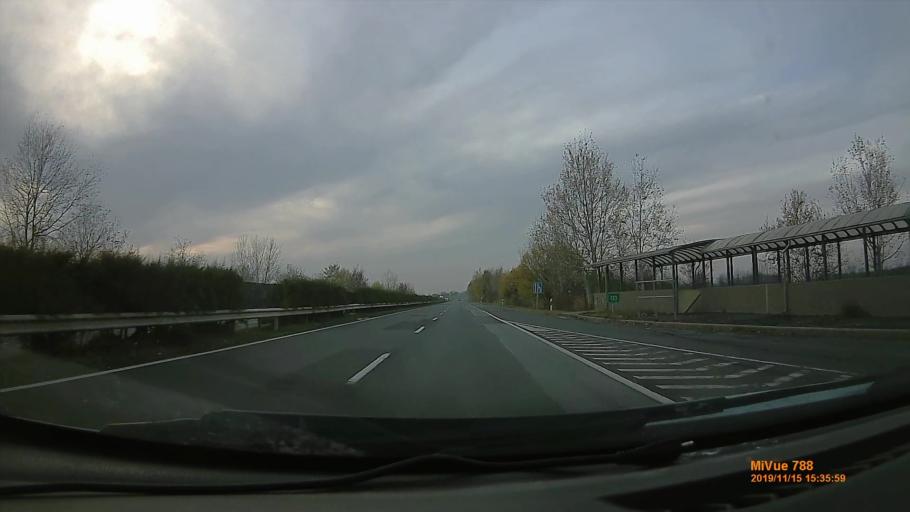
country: HU
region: Bekes
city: Gyula
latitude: 46.6560
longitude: 21.2202
